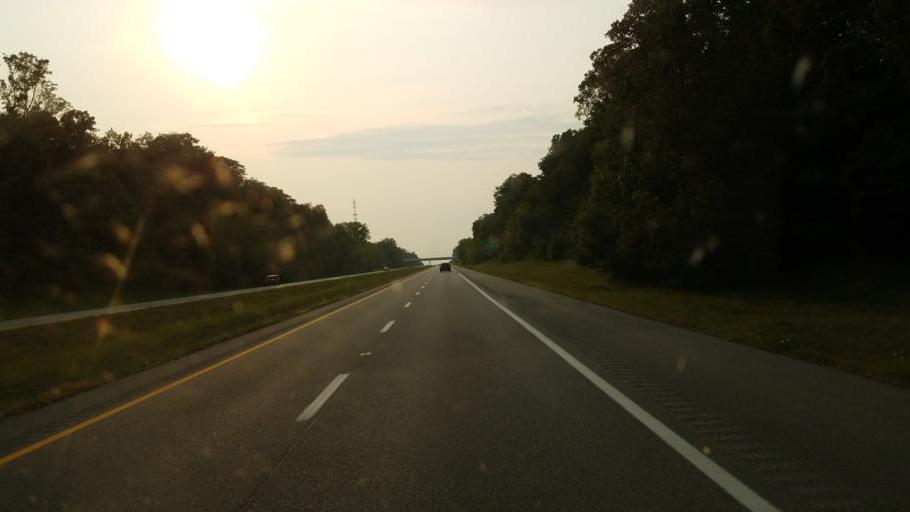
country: US
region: Ohio
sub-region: Geauga County
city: Bainbridge
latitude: 41.3848
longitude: -81.3149
